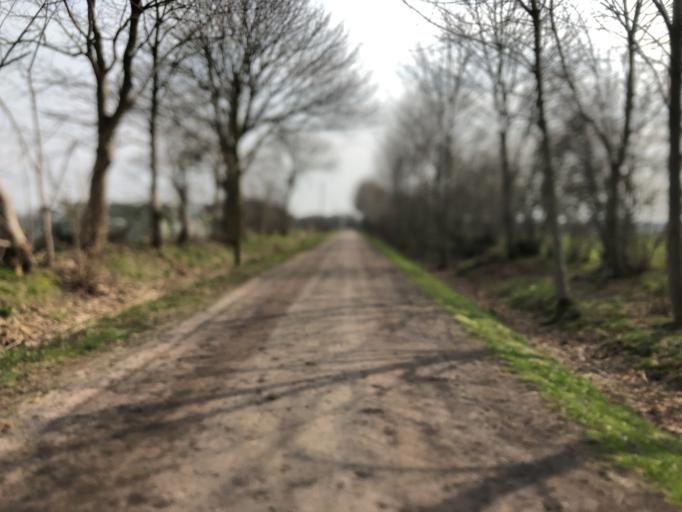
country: DE
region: Schleswig-Holstein
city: Wanderup
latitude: 54.6877
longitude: 9.3014
